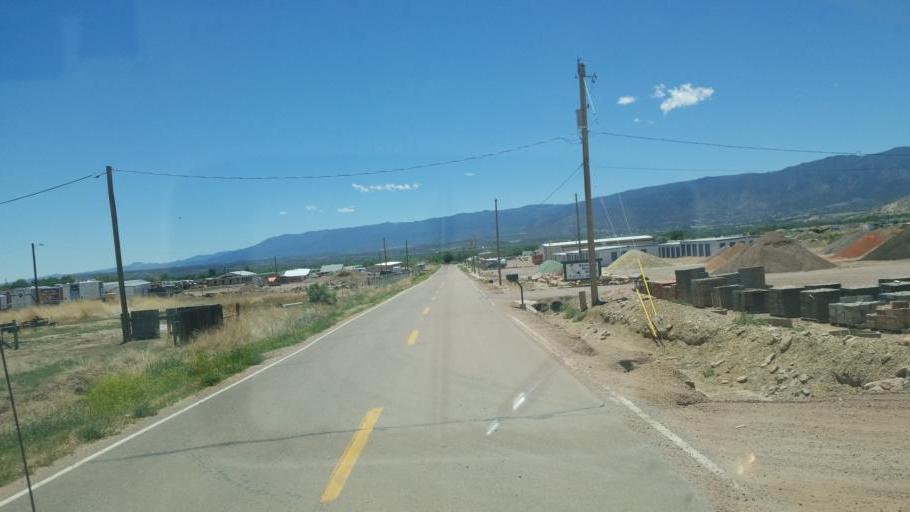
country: US
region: Colorado
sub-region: Fremont County
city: Canon City
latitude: 38.4756
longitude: -105.2226
